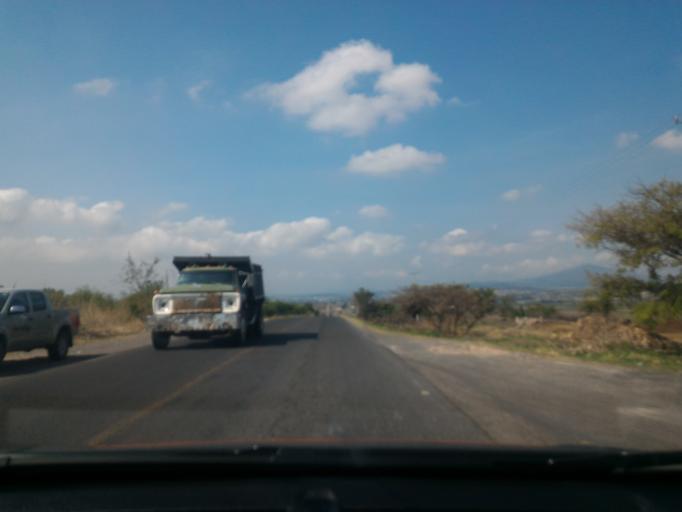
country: MX
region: Guanajuato
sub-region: Penjamo
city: Estacion la Piedad
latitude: 20.4302
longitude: -101.9905
